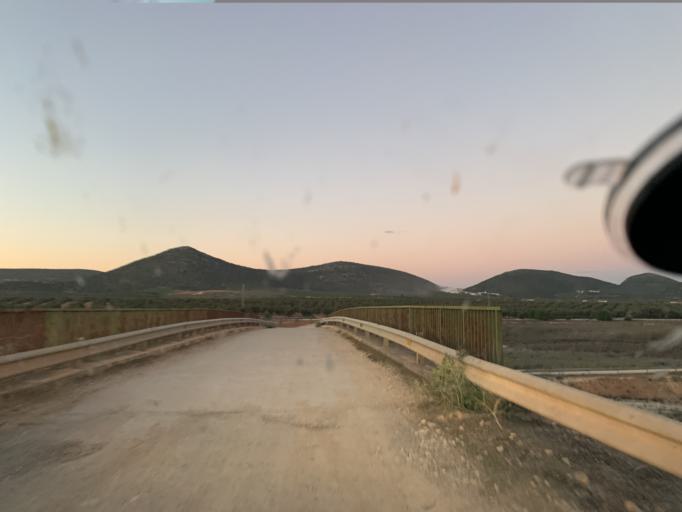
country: ES
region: Andalusia
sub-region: Provincia de Sevilla
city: Pedrera
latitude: 37.2126
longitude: -4.8515
